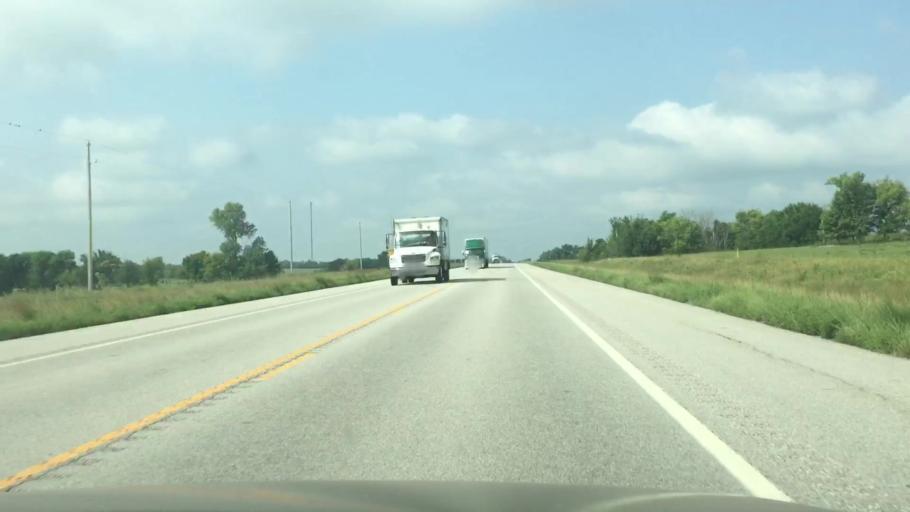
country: US
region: Kansas
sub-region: Miami County
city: Osawatomie
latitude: 38.4147
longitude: -95.0430
